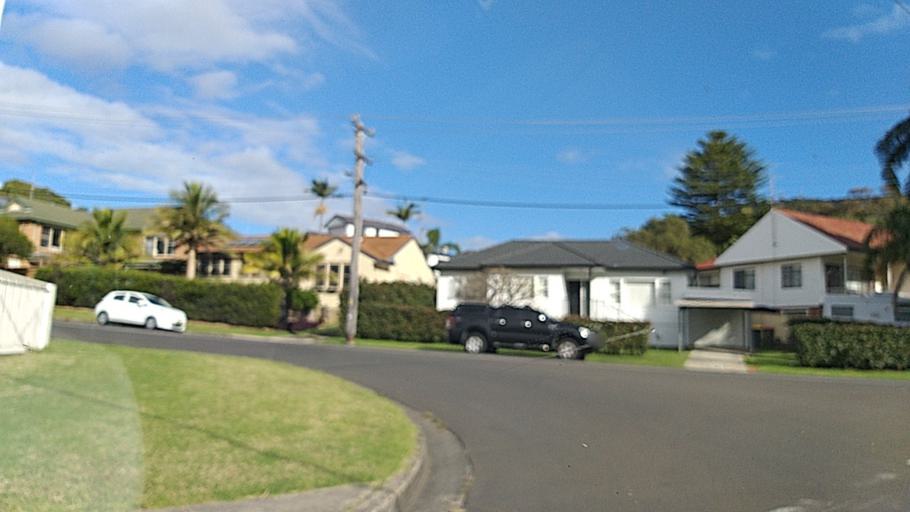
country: AU
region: New South Wales
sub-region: Wollongong
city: Mount Ousley
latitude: -34.3962
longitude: 150.8804
